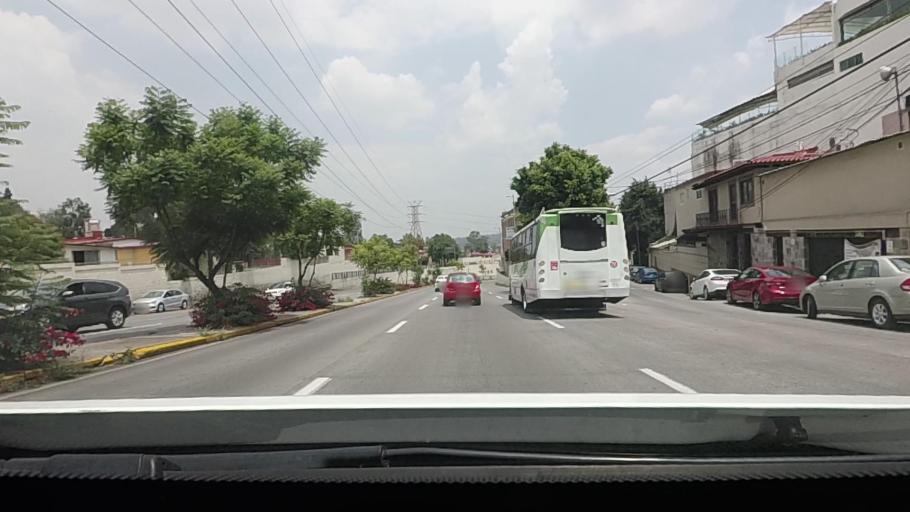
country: MX
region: Mexico
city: Naucalpan de Juarez
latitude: 19.4986
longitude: -99.2497
